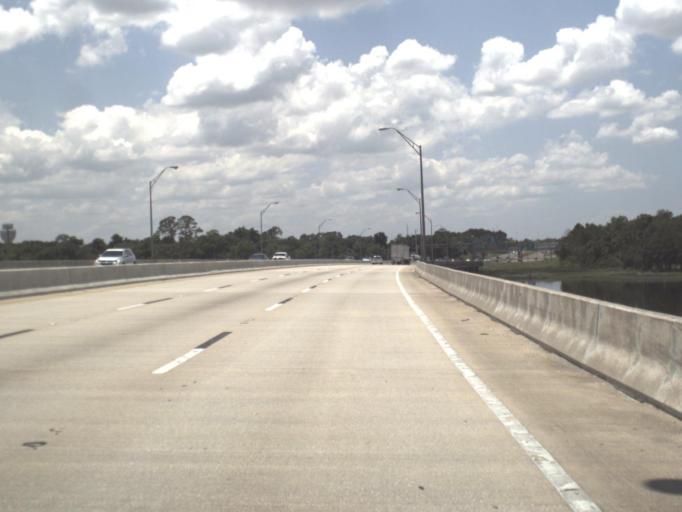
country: US
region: Florida
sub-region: Duval County
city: Jacksonville
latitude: 30.3687
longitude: -81.5517
